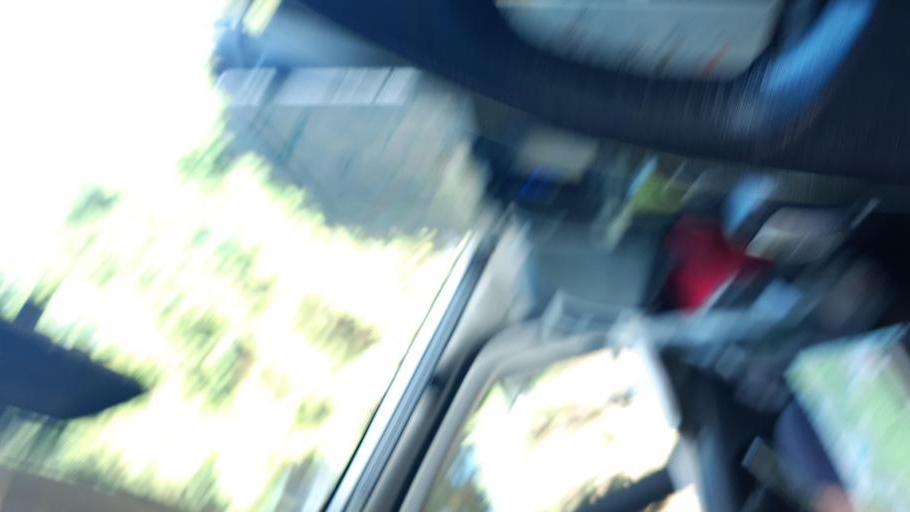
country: NZ
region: Southland
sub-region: Southland District
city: Winton
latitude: -45.7838
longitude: 168.1744
